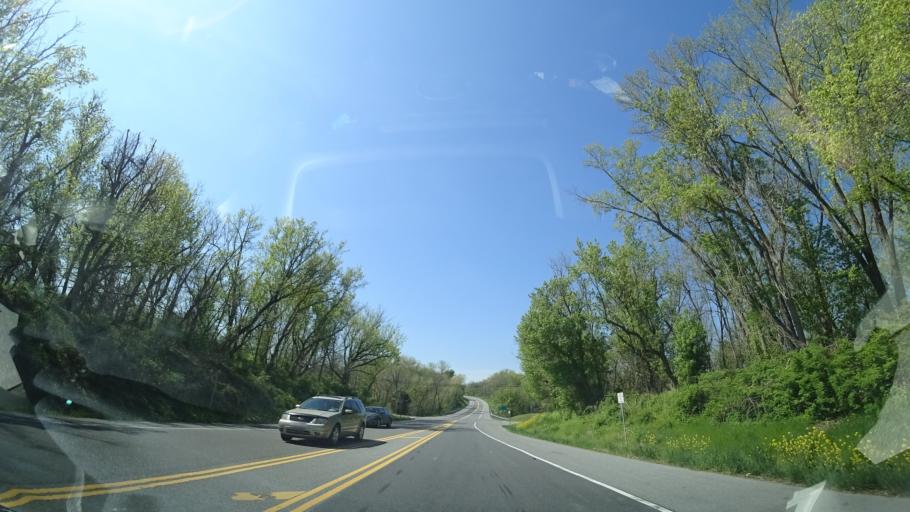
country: US
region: Maryland
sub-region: Washington County
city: Robinwood
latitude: 39.5839
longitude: -77.6415
